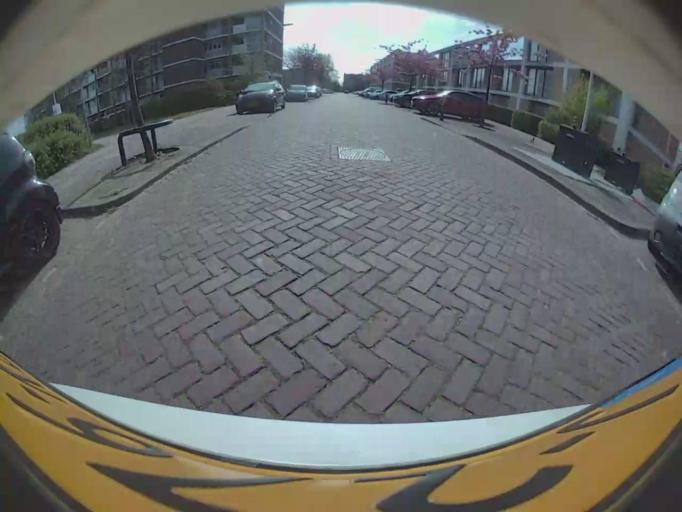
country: NL
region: South Holland
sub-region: Gemeente Westland
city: Kwintsheul
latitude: 52.0461
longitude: 4.2623
